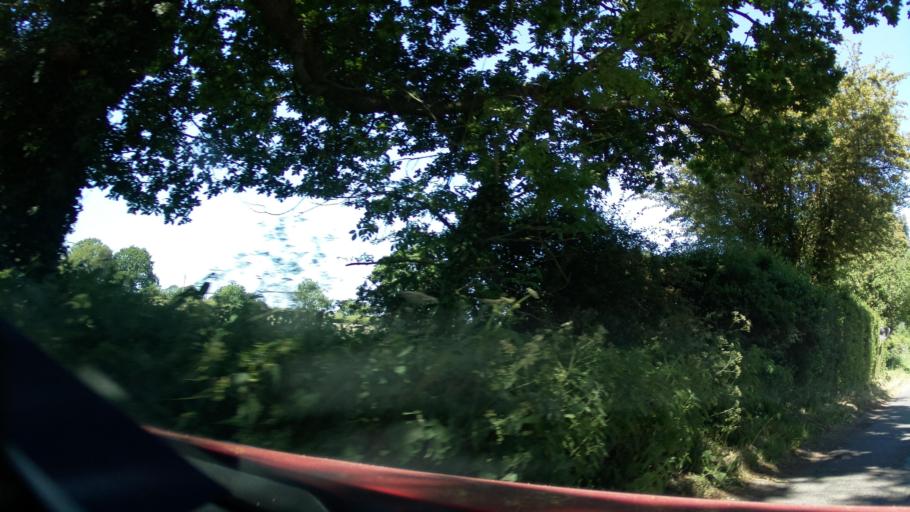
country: GB
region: England
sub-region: Wiltshire
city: Lyneham
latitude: 51.4773
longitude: -1.9520
